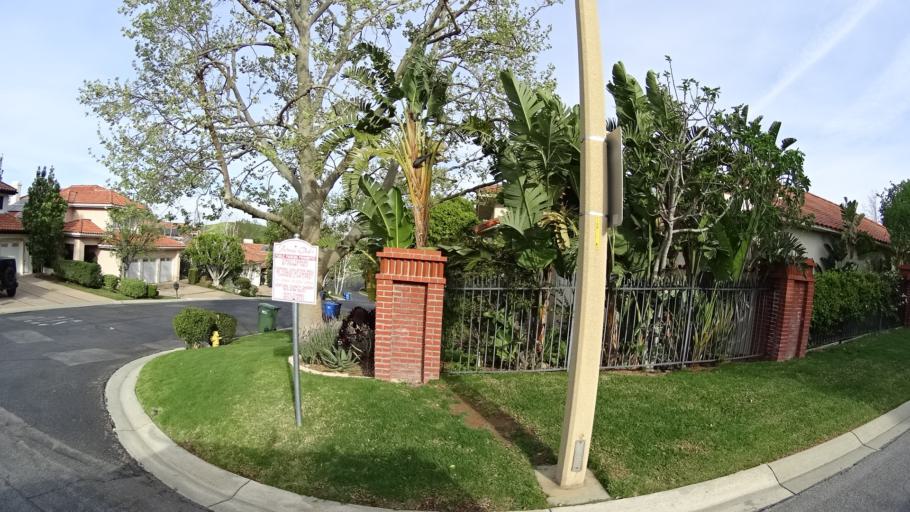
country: US
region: California
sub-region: Ventura County
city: Thousand Oaks
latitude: 34.1963
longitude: -118.8096
